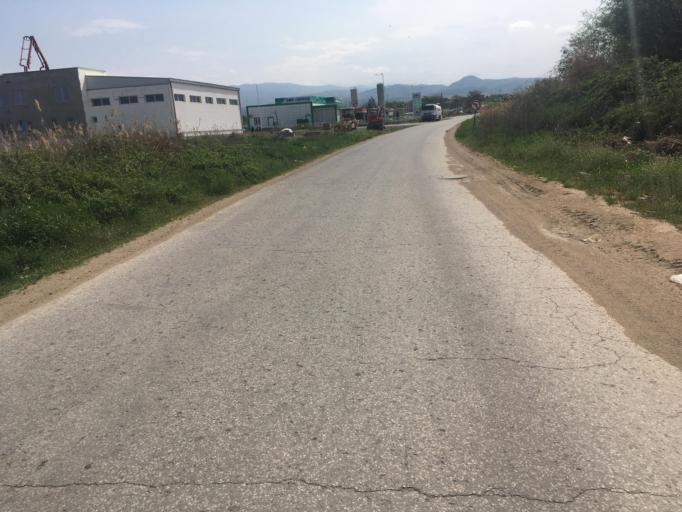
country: MK
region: Karbinci
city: Karbinci
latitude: 41.8003
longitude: 22.2177
